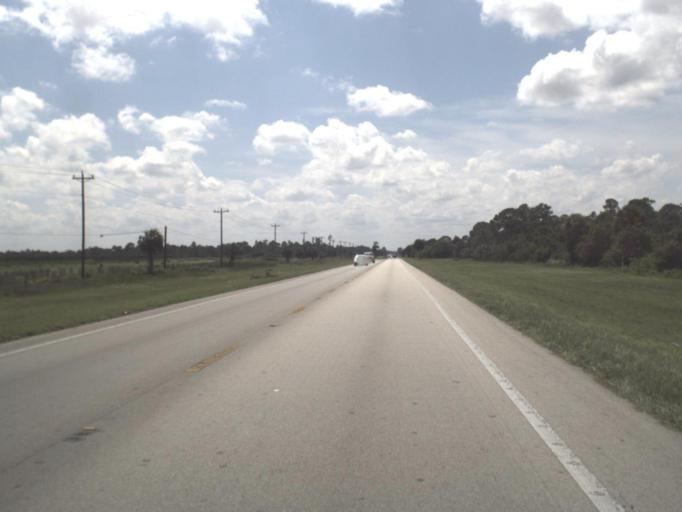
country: US
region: Florida
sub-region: Collier County
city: Immokalee
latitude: 26.4553
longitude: -81.4342
